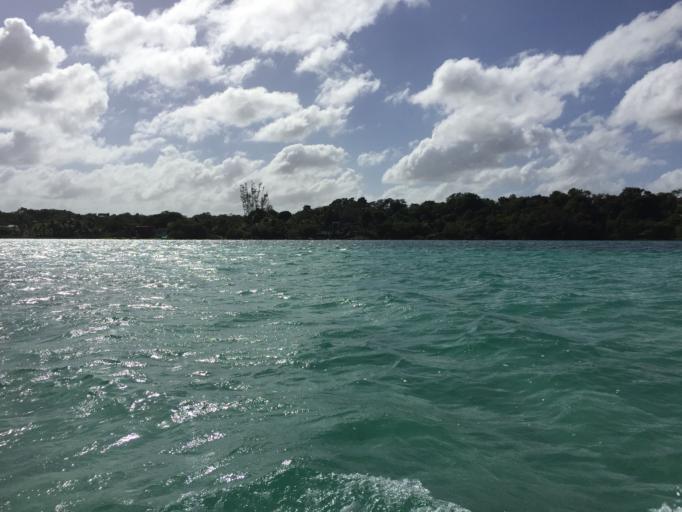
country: MX
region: Quintana Roo
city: Bacalar
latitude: 18.6503
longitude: -88.4083
